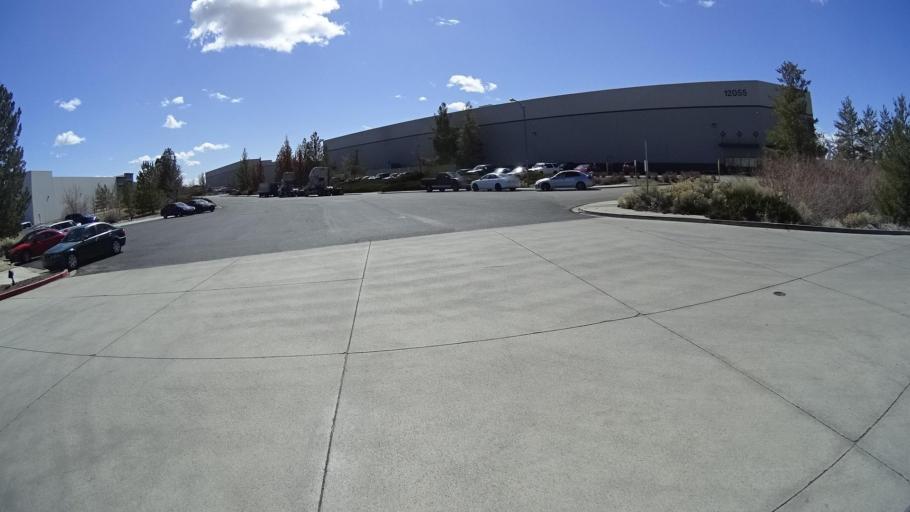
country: US
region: Nevada
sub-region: Washoe County
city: Lemmon Valley
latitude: 39.6481
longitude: -119.8628
